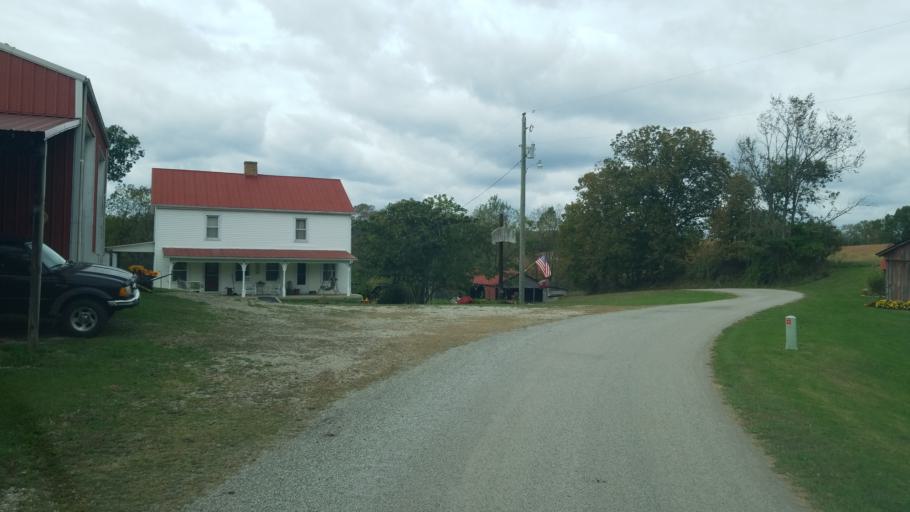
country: US
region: Ohio
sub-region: Jackson County
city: Wellston
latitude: 39.1695
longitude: -82.5624
